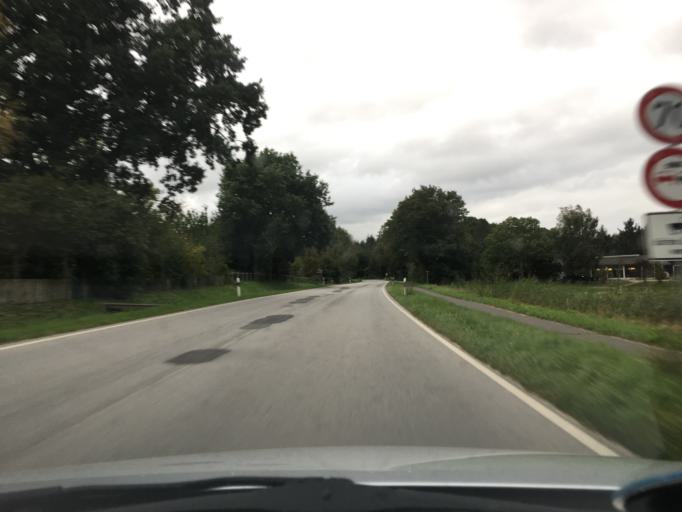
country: DE
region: Schleswig-Holstein
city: Neudorf-Bornstein
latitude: 54.4491
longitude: 9.9254
